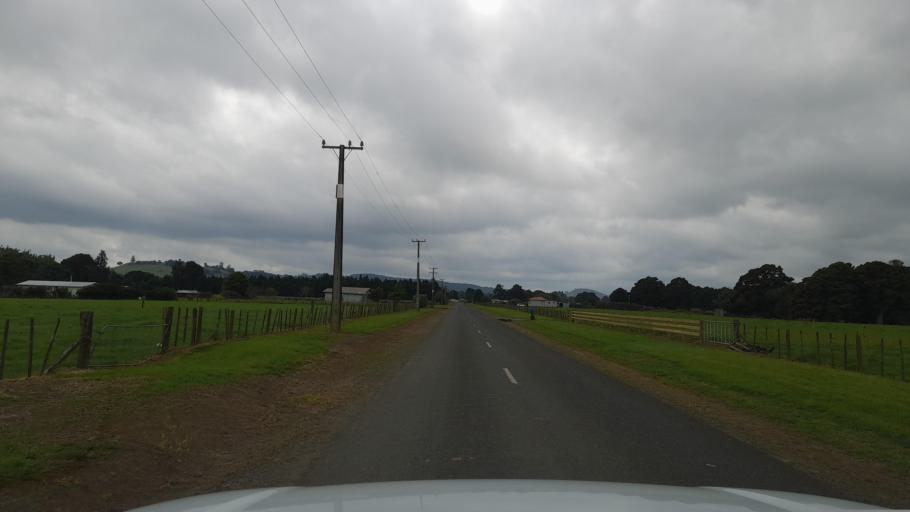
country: NZ
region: Northland
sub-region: Far North District
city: Waimate North
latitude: -35.4292
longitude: 173.7937
